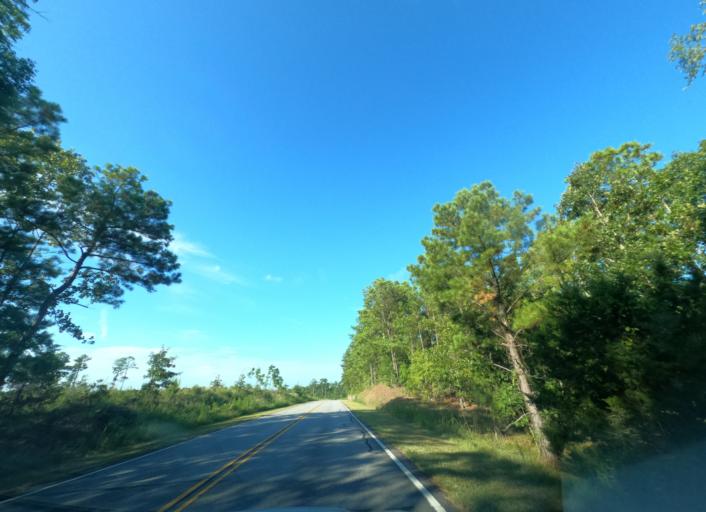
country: US
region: South Carolina
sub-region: McCormick County
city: McCormick
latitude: 33.8874
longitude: -82.4058
